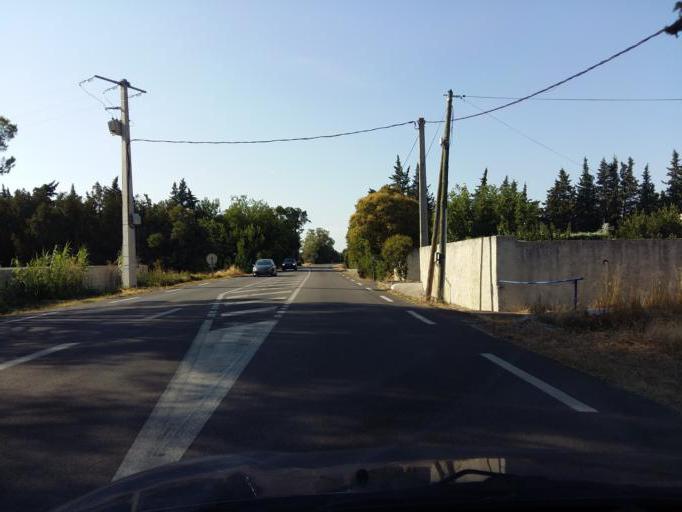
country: FR
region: Provence-Alpes-Cote d'Azur
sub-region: Departement du Vaucluse
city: Monteux
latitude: 44.0127
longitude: 5.0092
